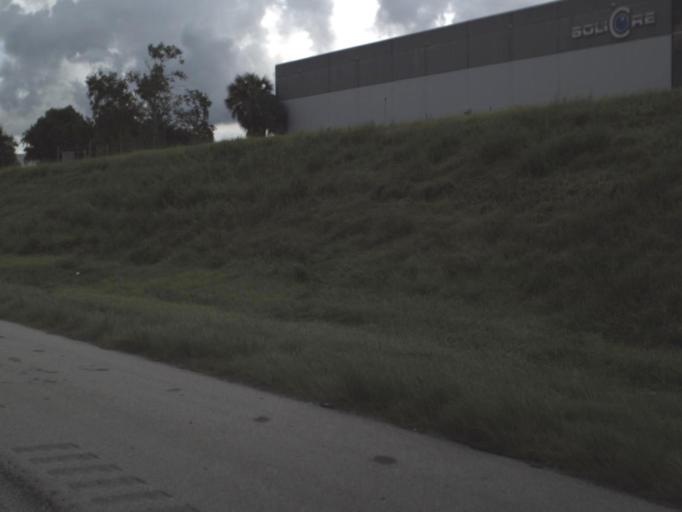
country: US
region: Florida
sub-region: Polk County
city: Gibsonia
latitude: 28.0790
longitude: -81.9783
